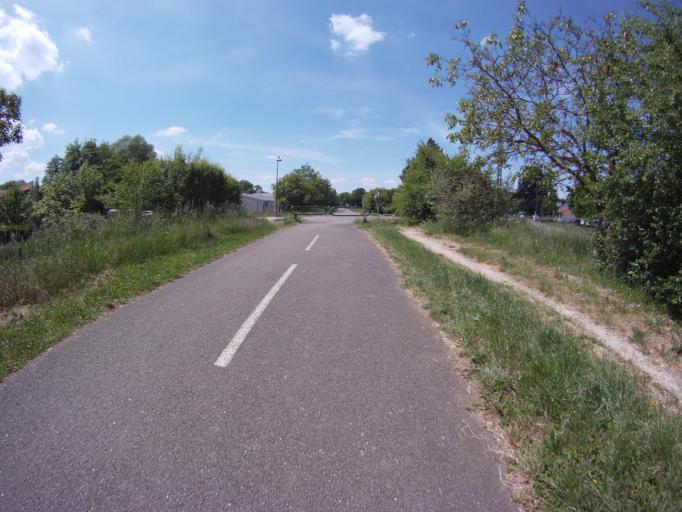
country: FR
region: Lorraine
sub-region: Departement de Meurthe-et-Moselle
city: Lay-Saint-Christophe
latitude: 48.7458
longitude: 6.2055
